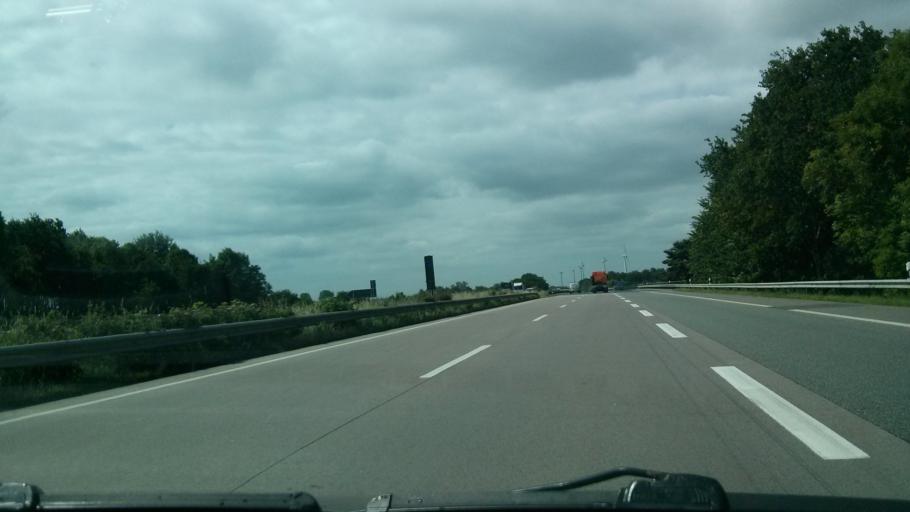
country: DE
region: Lower Saxony
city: Loxstedt
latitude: 53.4661
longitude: 8.6029
